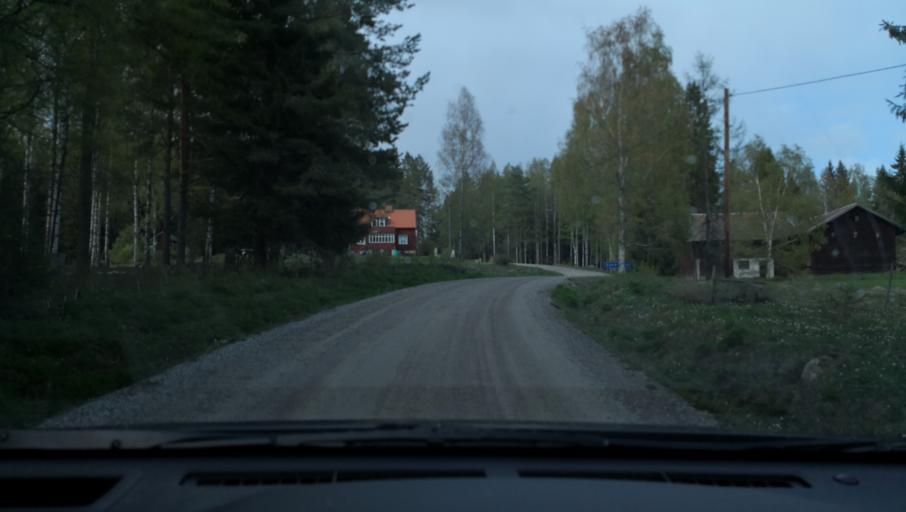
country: SE
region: Dalarna
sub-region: Saters Kommun
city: Saeter
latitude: 60.1794
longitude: 15.7257
